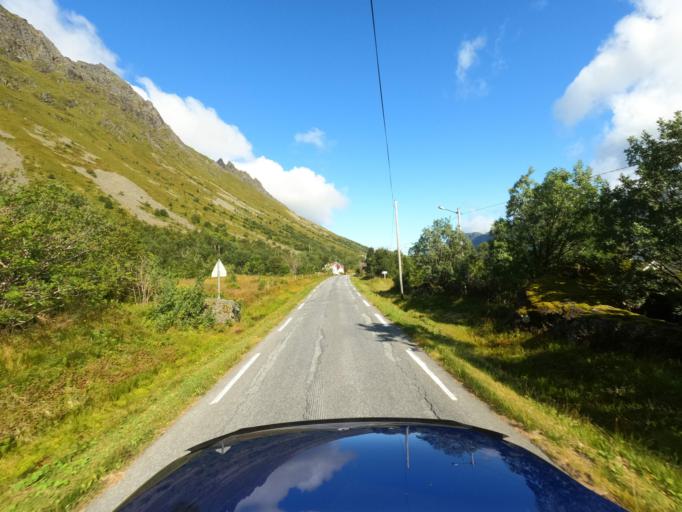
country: NO
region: Nordland
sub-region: Vagan
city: Kabelvag
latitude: 68.2712
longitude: 14.2506
